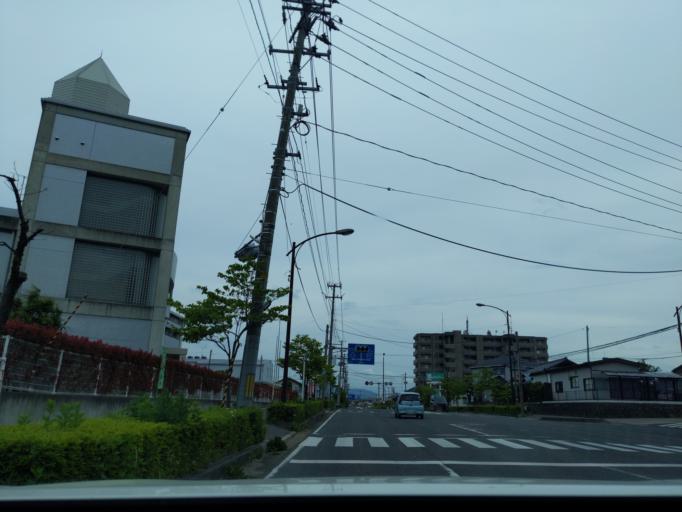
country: JP
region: Fukushima
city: Koriyama
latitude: 37.3643
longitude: 140.3652
